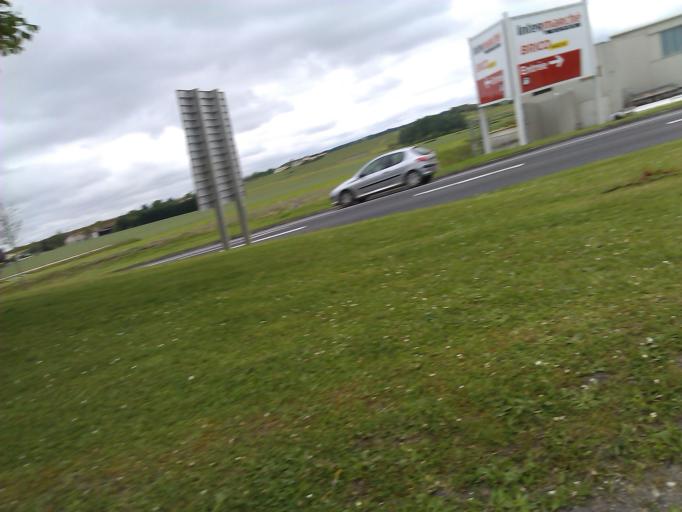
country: FR
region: Poitou-Charentes
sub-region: Departement de la Charente
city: Barbezieux-Saint-Hilaire
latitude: 45.4750
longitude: -0.1619
